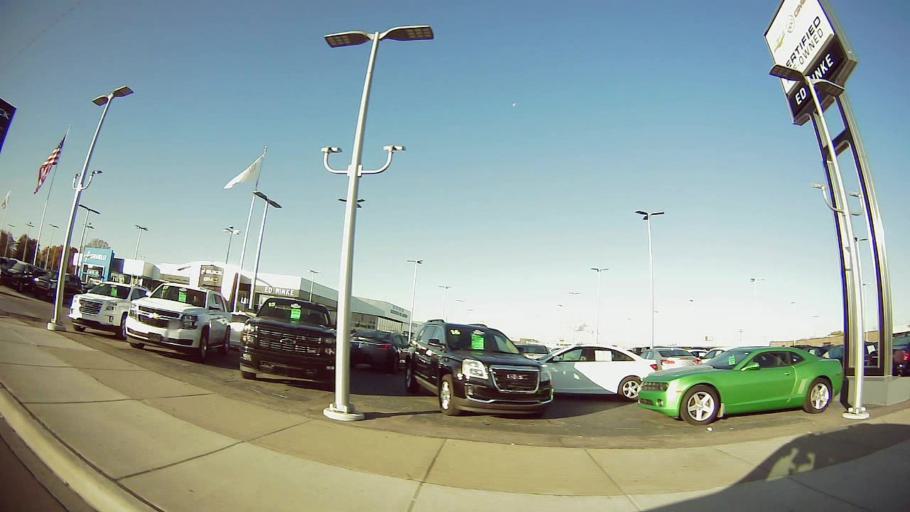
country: US
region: Michigan
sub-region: Macomb County
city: Center Line
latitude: 42.4866
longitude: -83.0277
